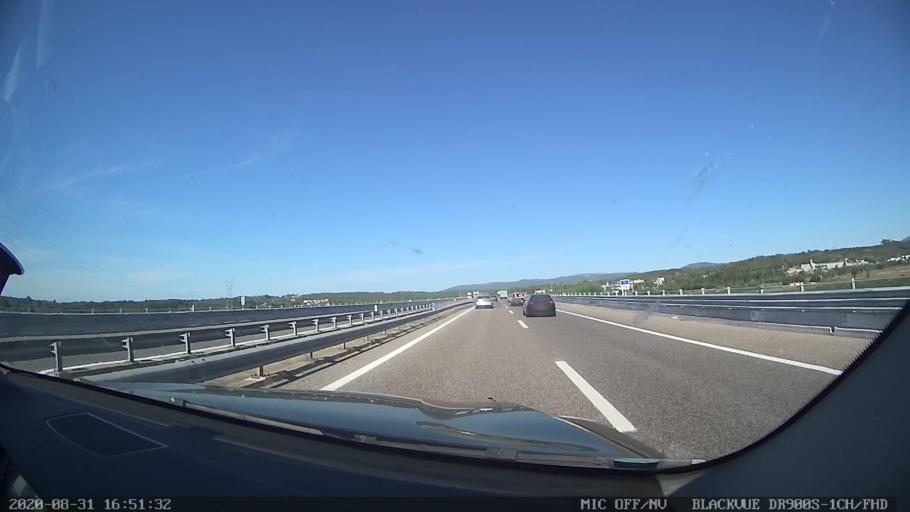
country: PT
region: Leiria
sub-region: Pombal
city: Pombal
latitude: 39.9732
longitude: -8.6409
